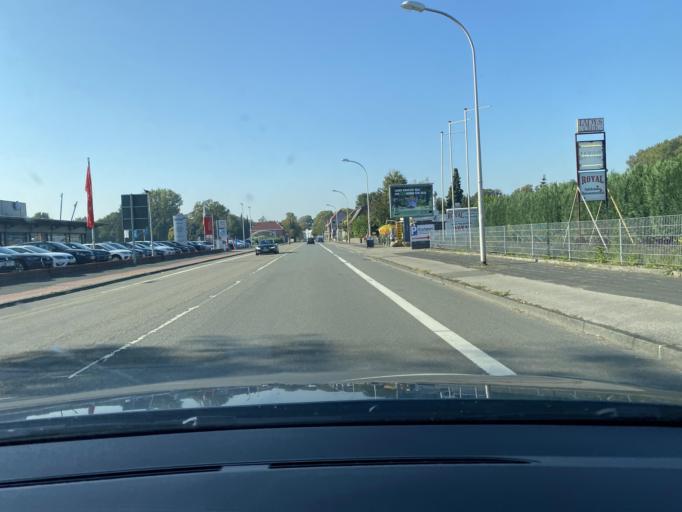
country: DE
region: North Rhine-Westphalia
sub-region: Regierungsbezirk Munster
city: Gronau
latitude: 52.2149
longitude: 6.9864
